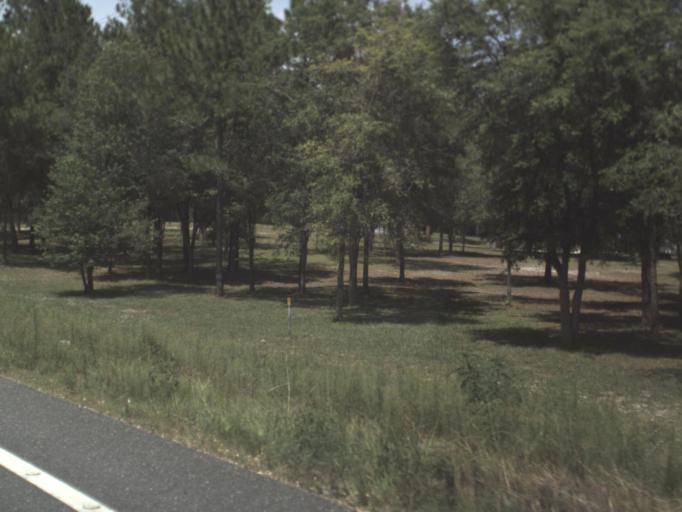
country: US
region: Florida
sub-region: Gilchrist County
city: Trenton
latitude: 29.8000
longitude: -82.8669
